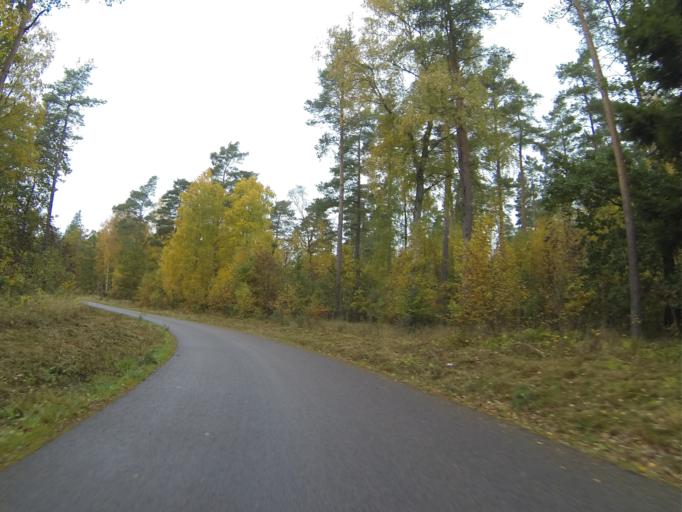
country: SE
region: Skane
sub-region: Sjobo Kommun
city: Sjoebo
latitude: 55.6381
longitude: 13.6657
